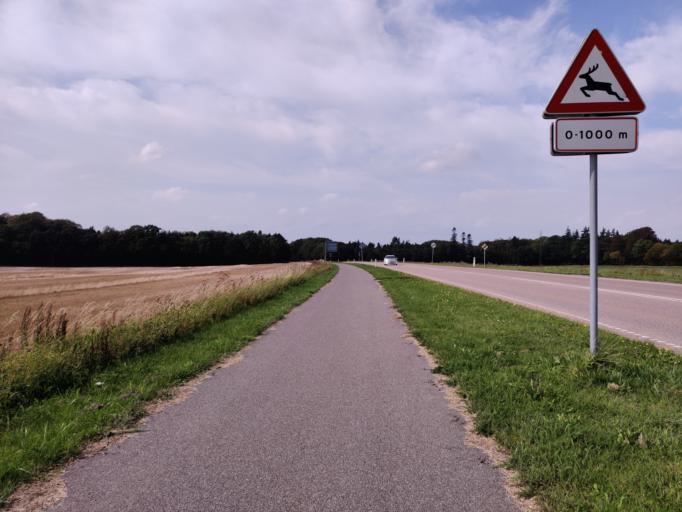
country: DK
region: Zealand
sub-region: Guldborgsund Kommune
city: Nykobing Falster
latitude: 54.7475
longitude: 11.9126
